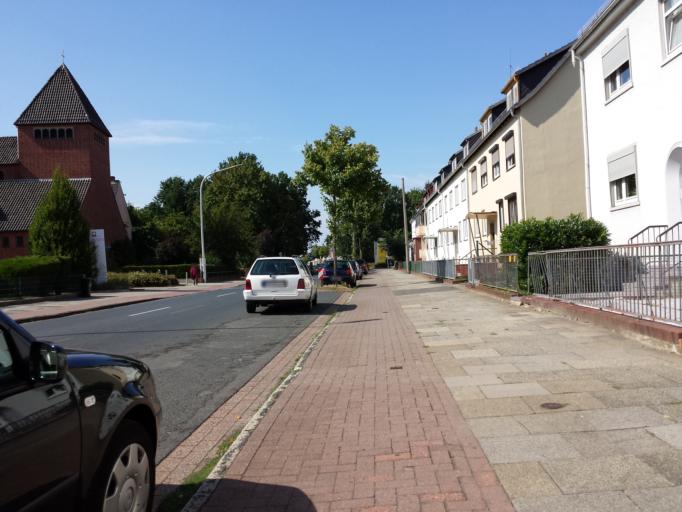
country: DE
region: Bremen
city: Bremen
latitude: 53.0539
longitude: 8.8161
